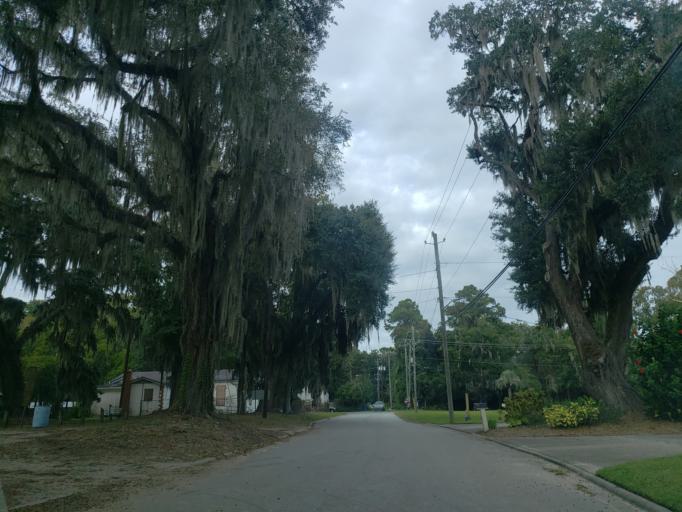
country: US
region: Georgia
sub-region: Chatham County
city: Montgomery
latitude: 31.9443
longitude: -81.1134
